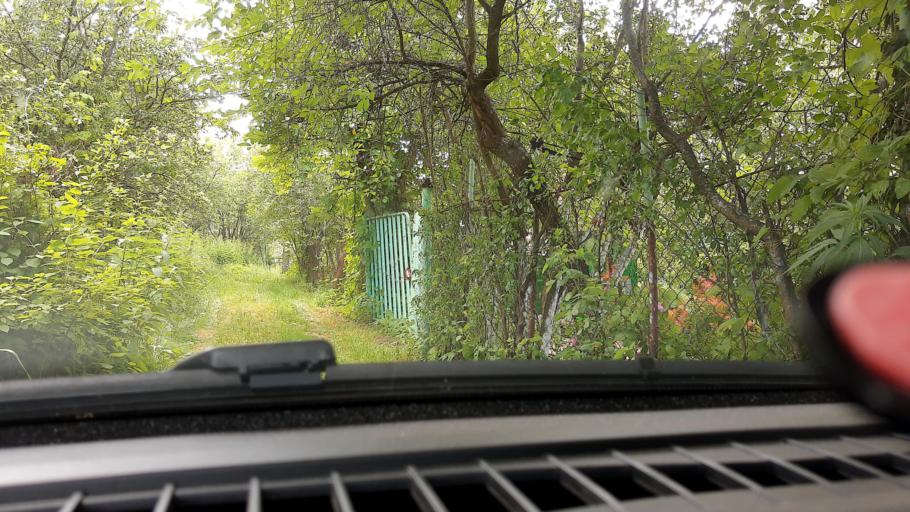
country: RU
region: Nizjnij Novgorod
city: Kstovo
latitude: 56.1423
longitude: 44.1733
